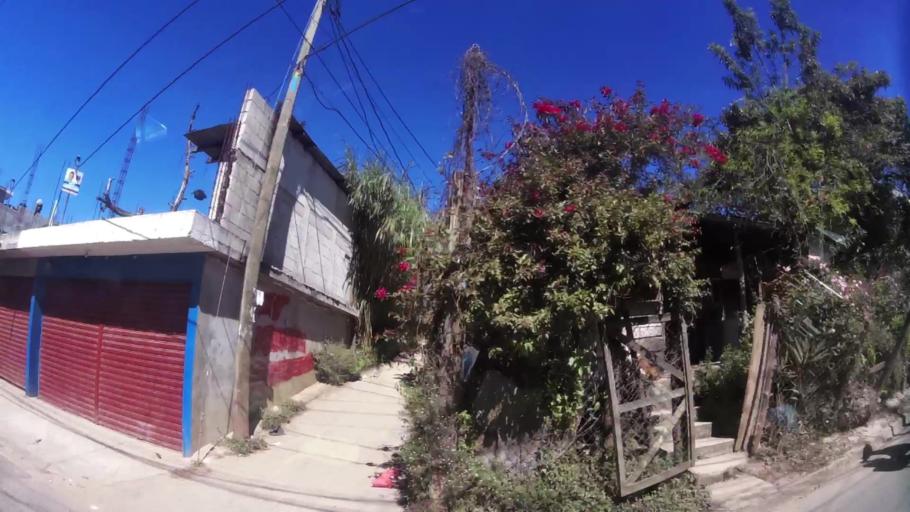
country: GT
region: Guatemala
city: San Jose Pinula
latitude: 14.5256
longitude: -90.4159
